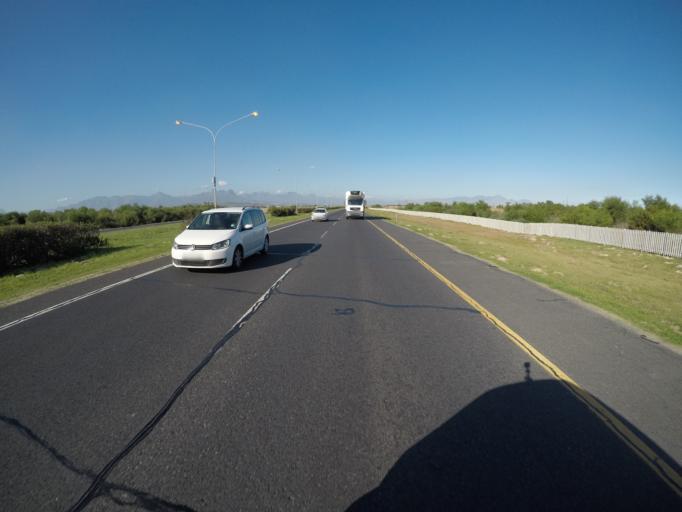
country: ZA
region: Western Cape
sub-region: City of Cape Town
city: Kraaifontein
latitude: -34.0322
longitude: 18.7046
